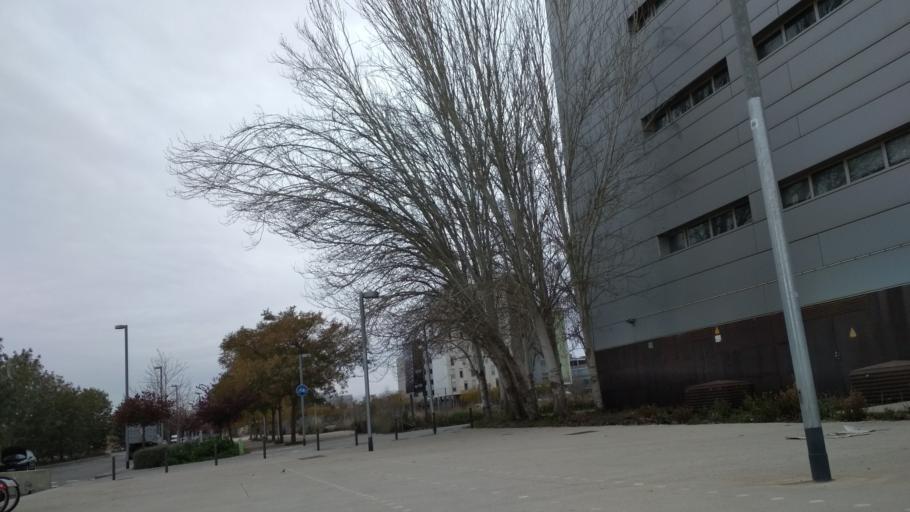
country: ES
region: Catalonia
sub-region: Provincia de Barcelona
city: Sants-Montjuic
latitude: 41.3510
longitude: 2.1450
